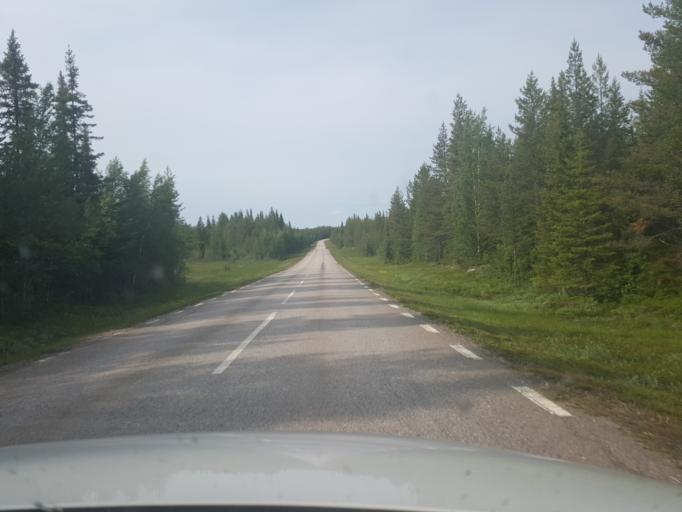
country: SE
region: Norrbotten
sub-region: Arjeplogs Kommun
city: Arjeplog
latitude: 65.8171
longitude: 18.0079
